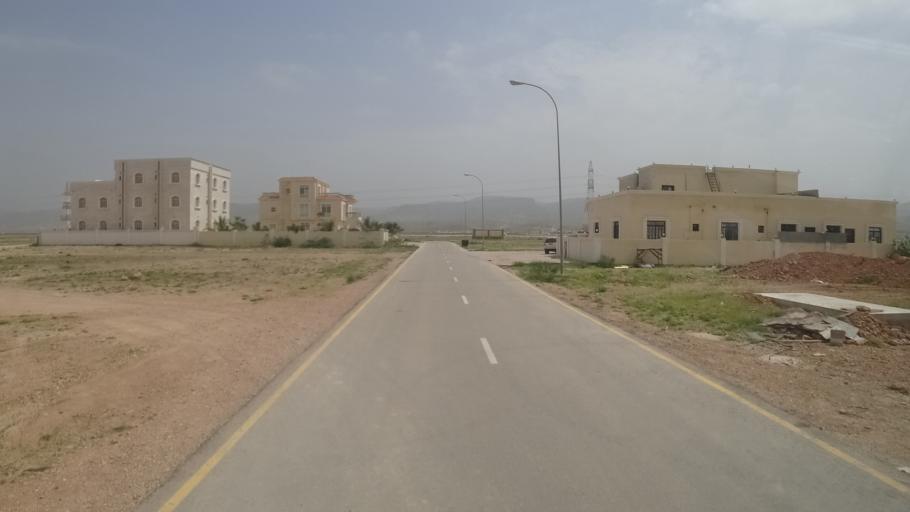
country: OM
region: Zufar
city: Salalah
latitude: 17.1014
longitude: 54.2145
